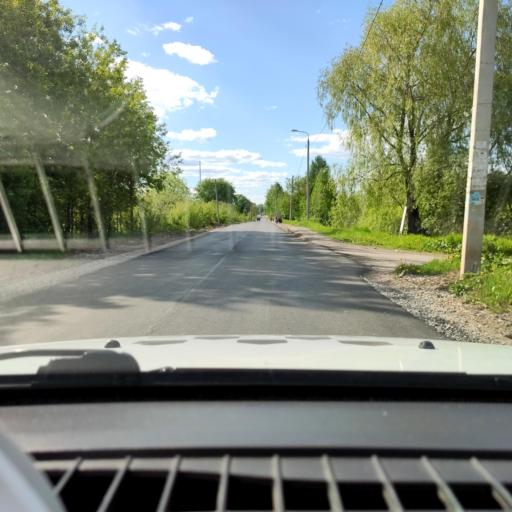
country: RU
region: Perm
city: Novyye Lyady
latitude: 58.0464
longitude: 56.6108
